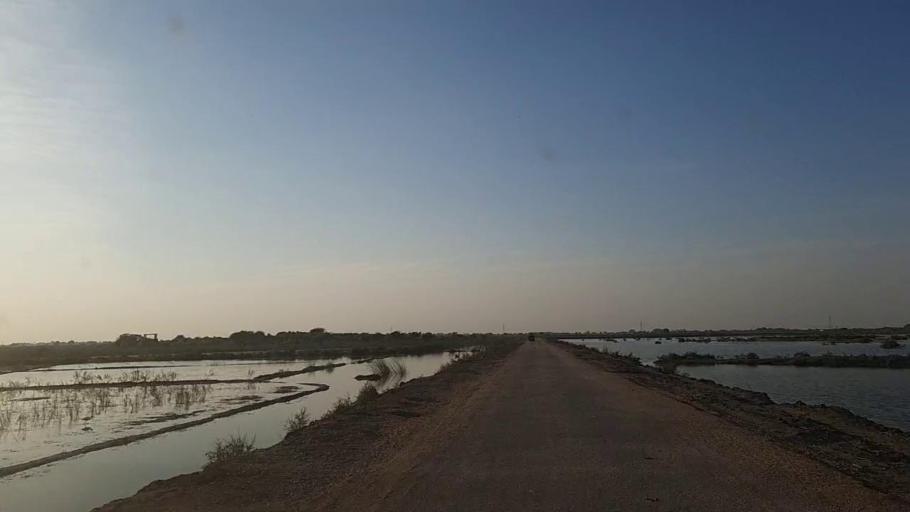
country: PK
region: Sindh
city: Mirpur Batoro
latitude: 24.6852
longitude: 68.2070
